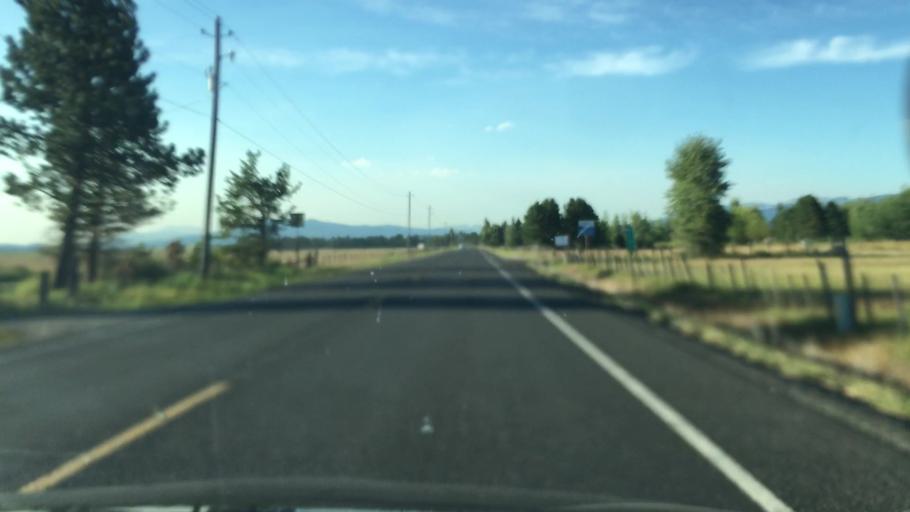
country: US
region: Idaho
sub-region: Valley County
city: McCall
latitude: 44.8124
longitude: -116.0781
